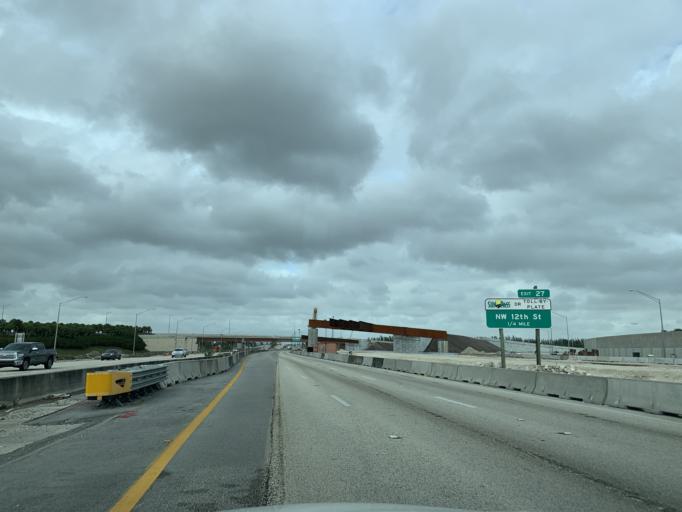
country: US
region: Florida
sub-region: Miami-Dade County
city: Sweetwater
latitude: 25.7725
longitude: -80.3853
